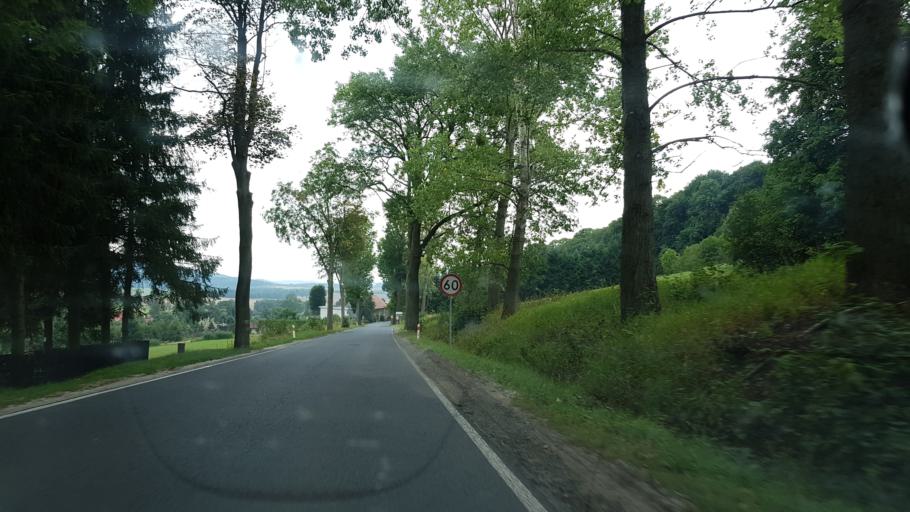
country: PL
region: Lower Silesian Voivodeship
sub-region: Powiat kamiennogorski
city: Marciszow
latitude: 50.8886
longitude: 15.9945
